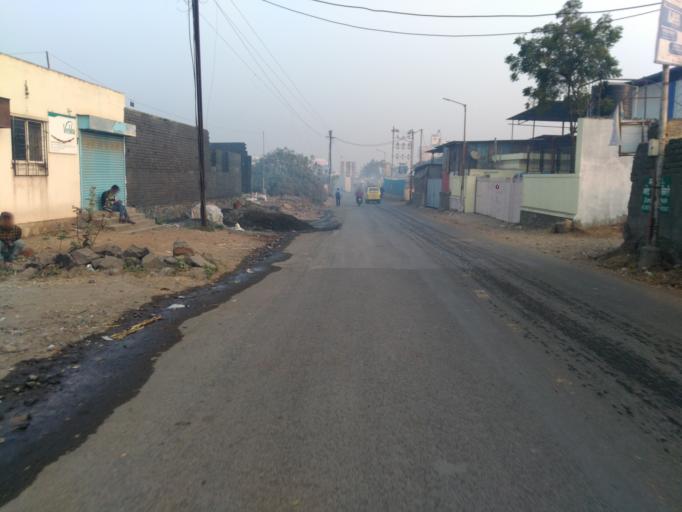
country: IN
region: Maharashtra
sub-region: Pune Division
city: Pune
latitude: 18.4462
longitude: 73.8856
